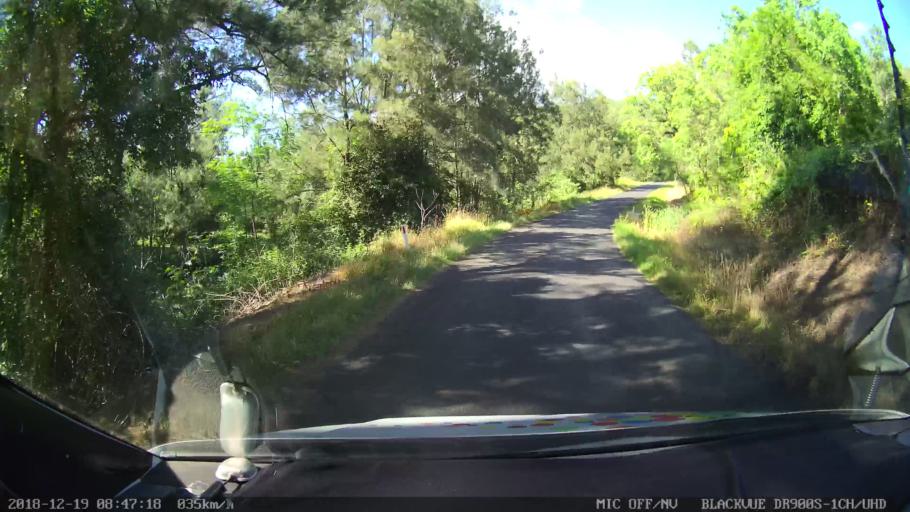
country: AU
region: New South Wales
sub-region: Kyogle
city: Kyogle
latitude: -28.3667
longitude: 152.9720
